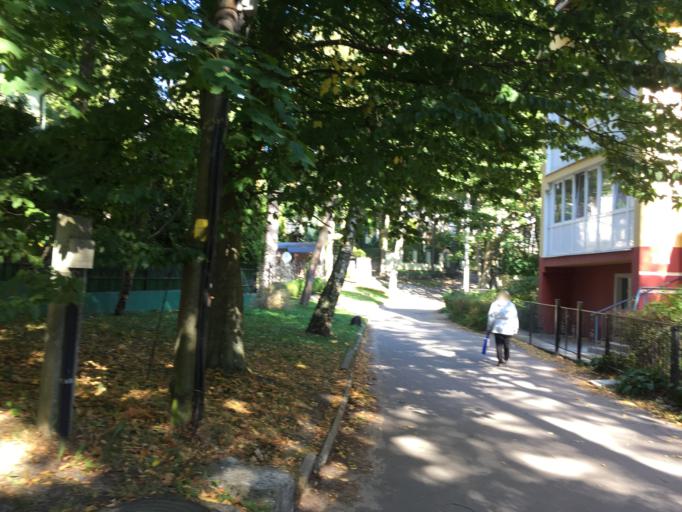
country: RU
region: Kaliningrad
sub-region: Gorod Svetlogorsk
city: Svetlogorsk
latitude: 54.9415
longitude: 20.1461
